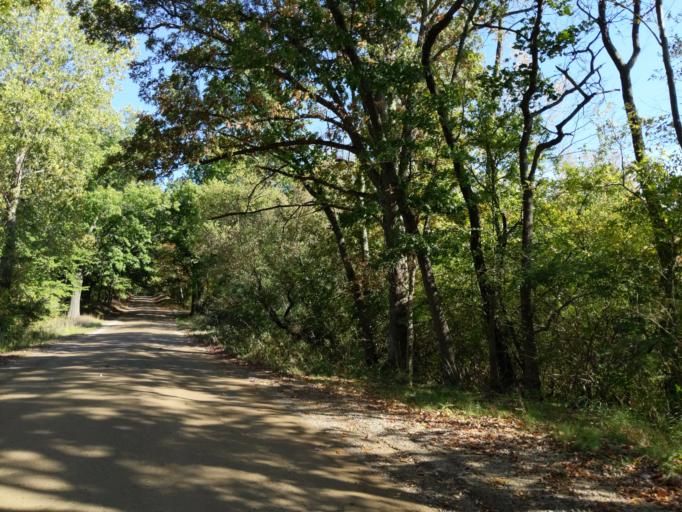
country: US
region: Michigan
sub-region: Clinton County
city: Bath
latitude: 42.8060
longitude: -84.4385
